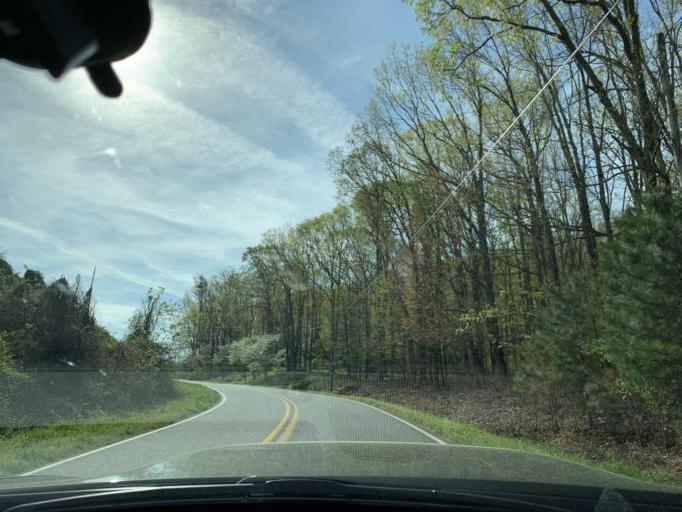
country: US
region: Georgia
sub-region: Forsyth County
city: Cumming
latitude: 34.2541
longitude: -84.1214
